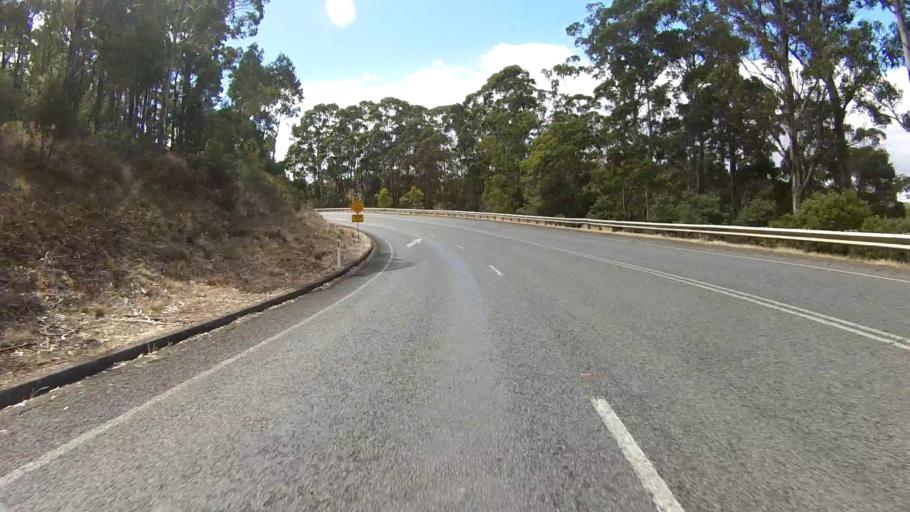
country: AU
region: Tasmania
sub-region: Sorell
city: Sorell
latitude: -42.6339
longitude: 147.6257
